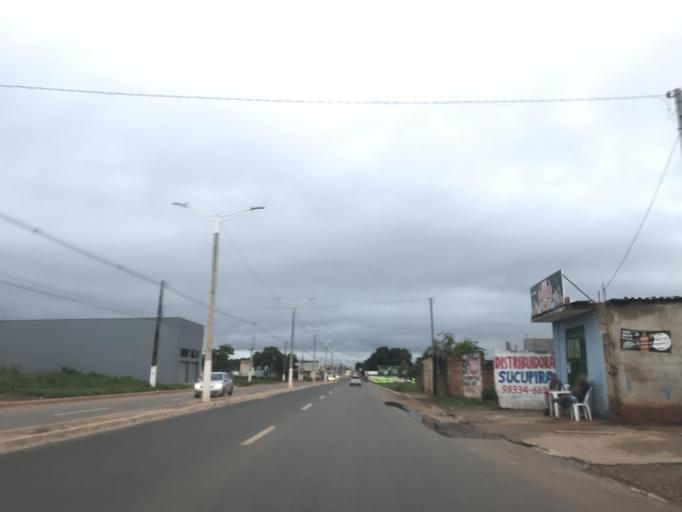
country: BR
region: Goias
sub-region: Luziania
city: Luziania
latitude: -16.2147
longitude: -47.9308
